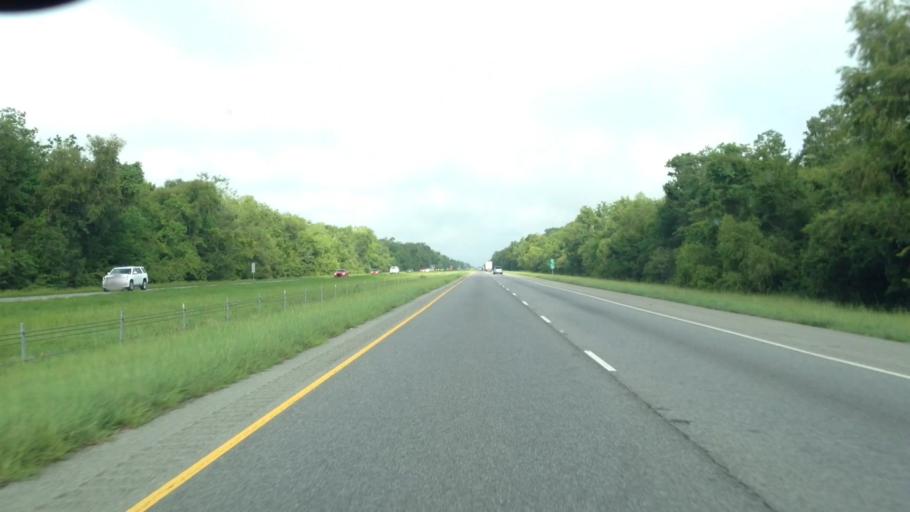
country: US
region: Louisiana
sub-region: Saint John the Baptist Parish
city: Garyville
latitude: 30.1158
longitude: -90.5964
